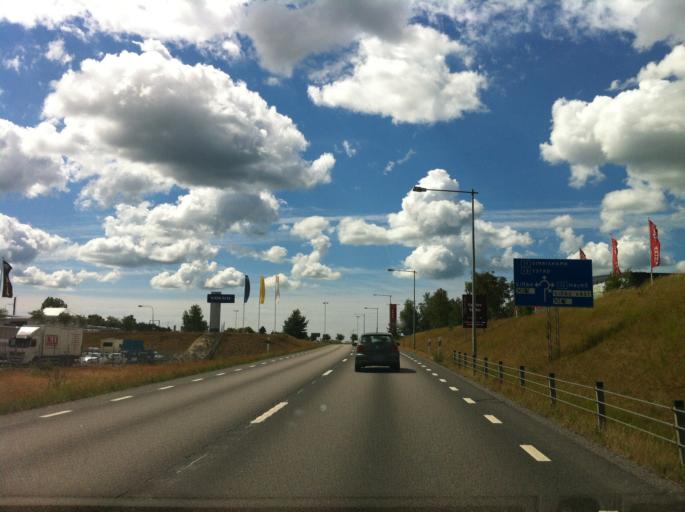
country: SE
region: Skane
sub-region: Sjobo Kommun
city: Sjoebo
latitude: 55.6415
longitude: 13.6852
